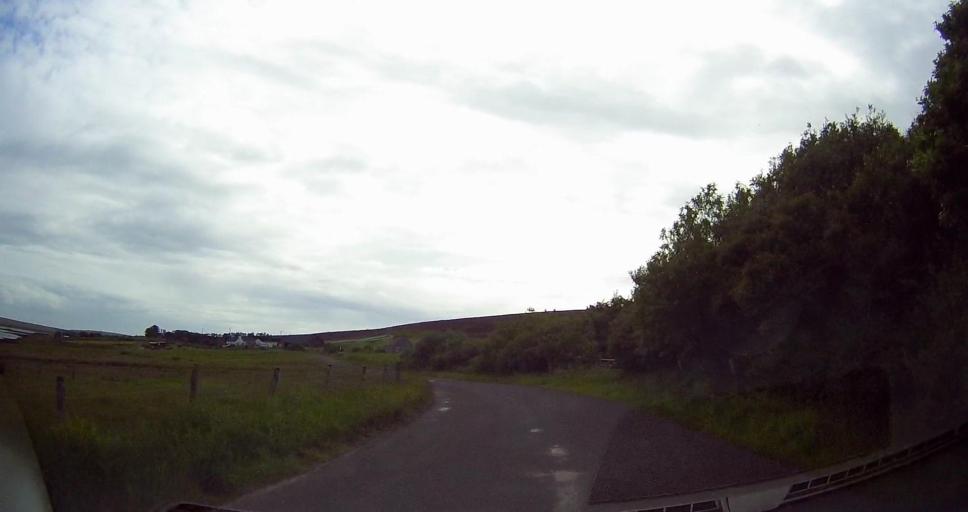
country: GB
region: Scotland
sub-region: Orkney Islands
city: Stromness
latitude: 58.8005
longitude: -3.2491
